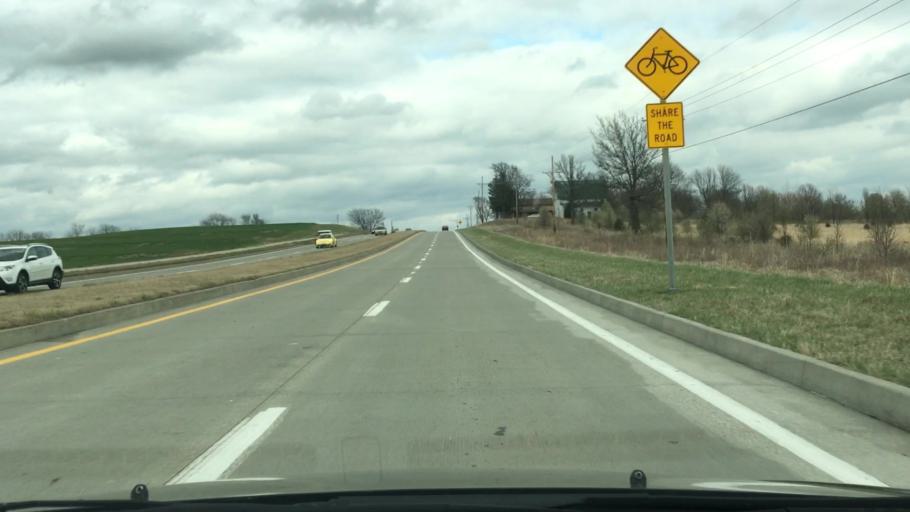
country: US
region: Missouri
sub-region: Cass County
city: Raymore
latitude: 38.8555
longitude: -94.4682
